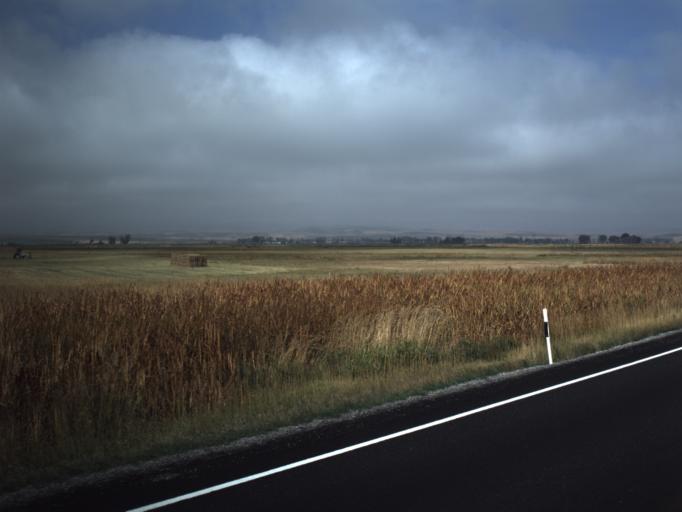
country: US
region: Utah
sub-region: Rich County
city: Randolph
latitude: 41.5096
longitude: -111.1295
